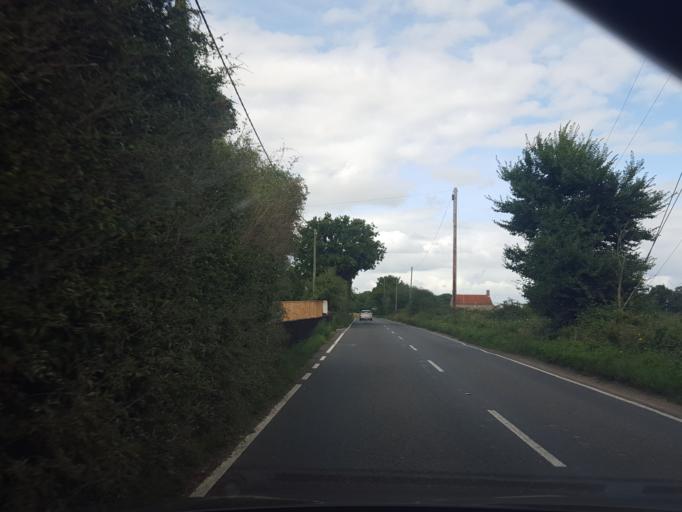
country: GB
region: England
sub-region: Essex
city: Mistley
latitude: 51.9231
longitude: 1.0846
